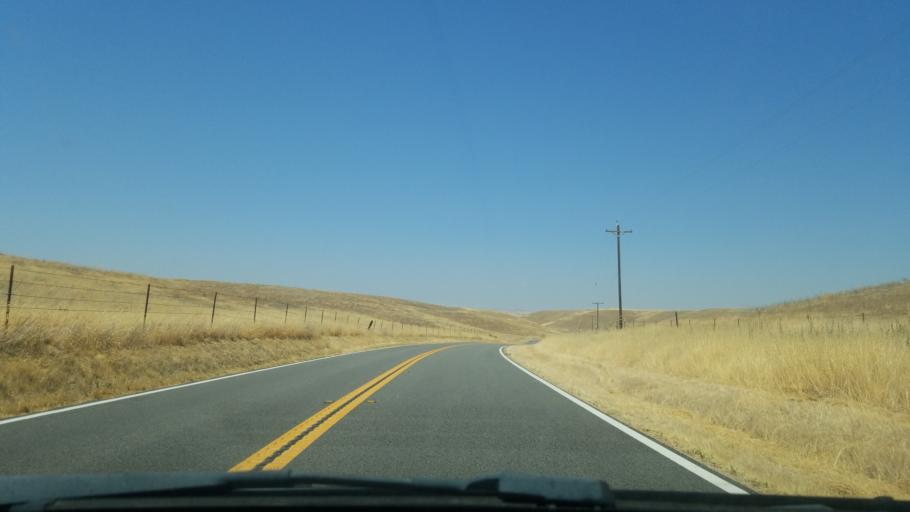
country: US
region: California
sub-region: San Luis Obispo County
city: Shandon
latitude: 35.6016
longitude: -120.4119
